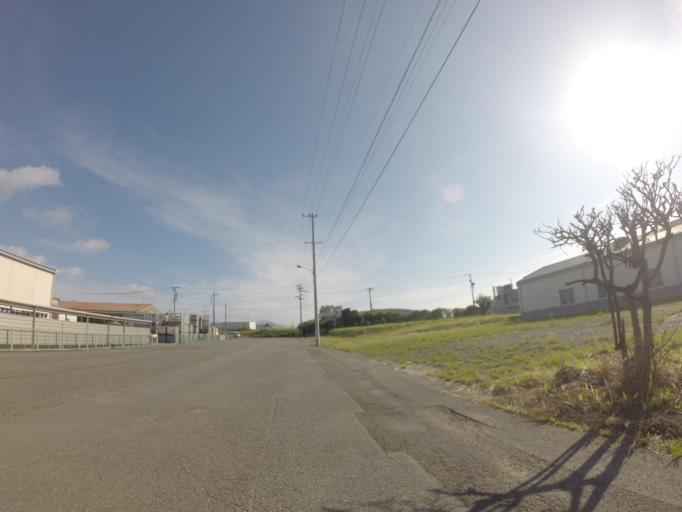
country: JP
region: Shizuoka
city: Yaizu
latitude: 34.8180
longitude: 138.3220
